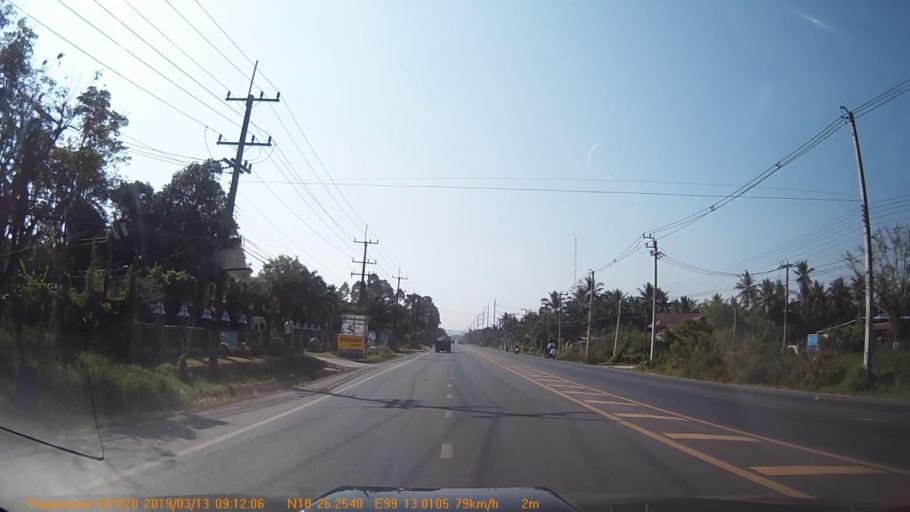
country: TH
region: Chumphon
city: Chumphon
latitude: 10.4373
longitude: 99.2170
